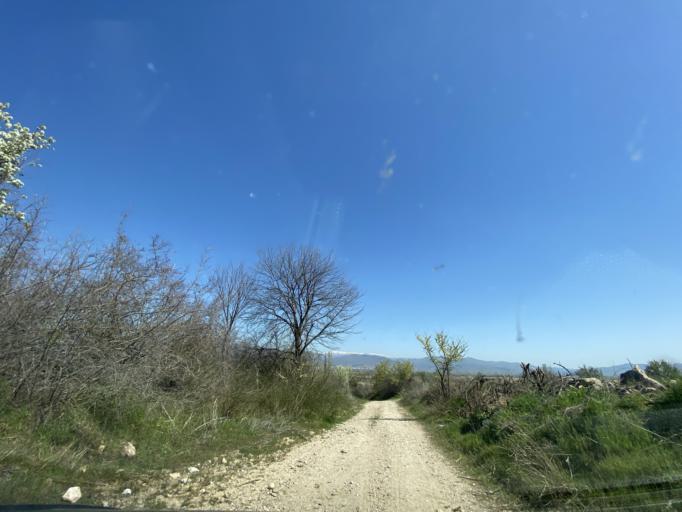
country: MK
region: Zrnovci
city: Zrnovci
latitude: 41.8534
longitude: 22.3896
